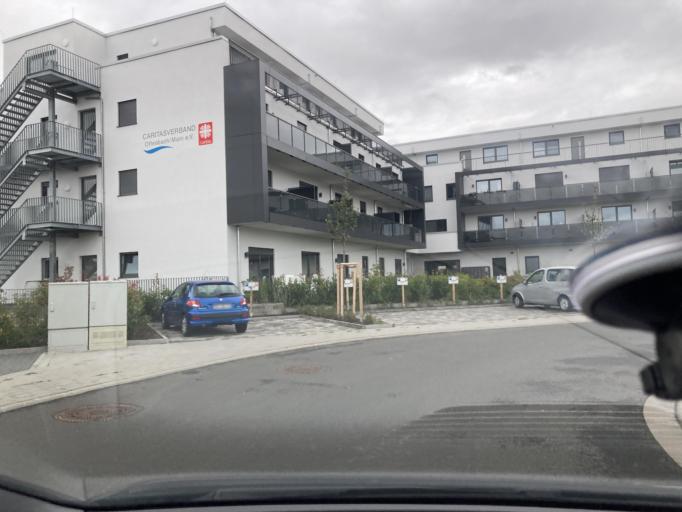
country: DE
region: Bavaria
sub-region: Regierungsbezirk Unterfranken
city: Kahl am Main
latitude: 50.0356
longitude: 9.0264
